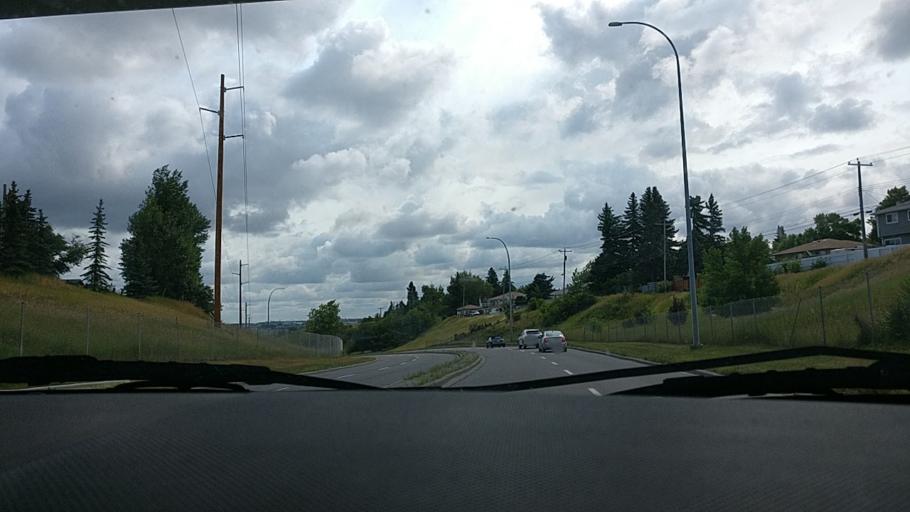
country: CA
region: Alberta
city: Calgary
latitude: 51.0961
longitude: -114.0783
